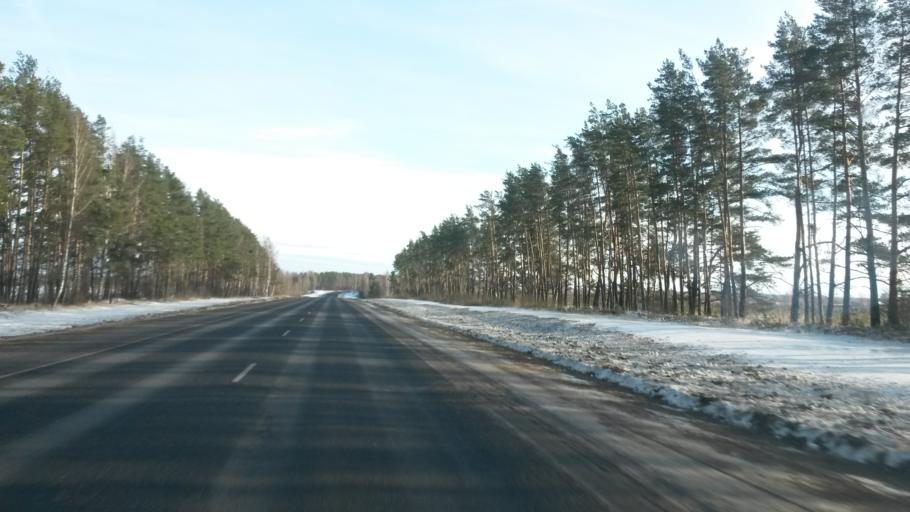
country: RU
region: Jaroslavl
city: Levashevo
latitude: 57.6426
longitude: 40.4955
